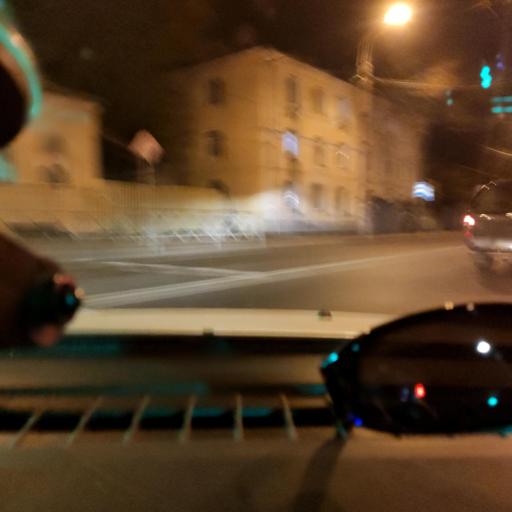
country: RU
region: Samara
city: Rozhdestveno
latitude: 53.1801
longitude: 50.0765
